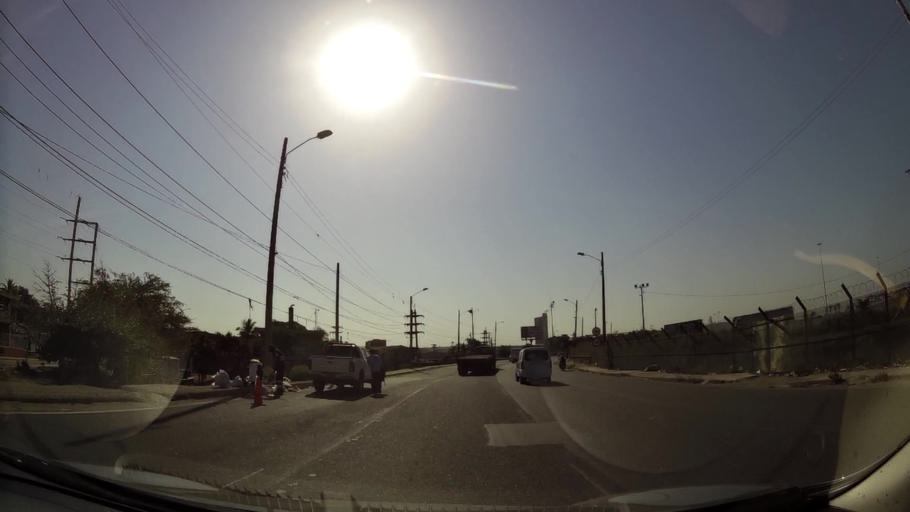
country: CO
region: Bolivar
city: Cartagena
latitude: 10.3844
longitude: -75.5068
